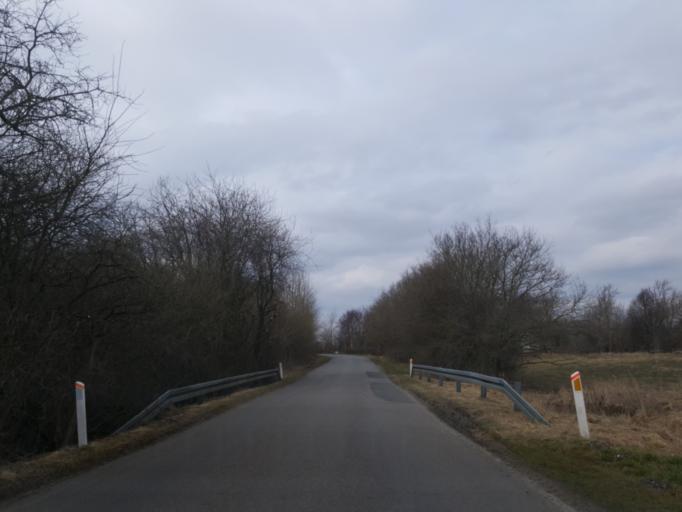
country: DK
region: Central Jutland
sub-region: Holstebro Kommune
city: Ulfborg
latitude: 56.3675
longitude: 8.2354
